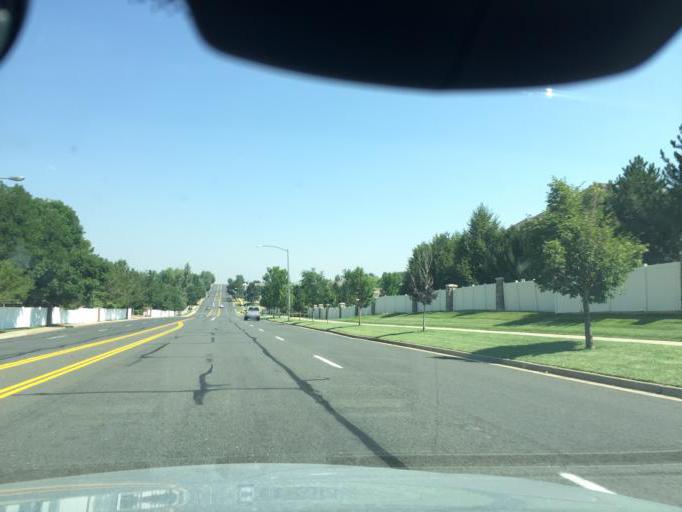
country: US
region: Colorado
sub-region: Adams County
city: Northglenn
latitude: 39.9013
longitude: -105.0061
